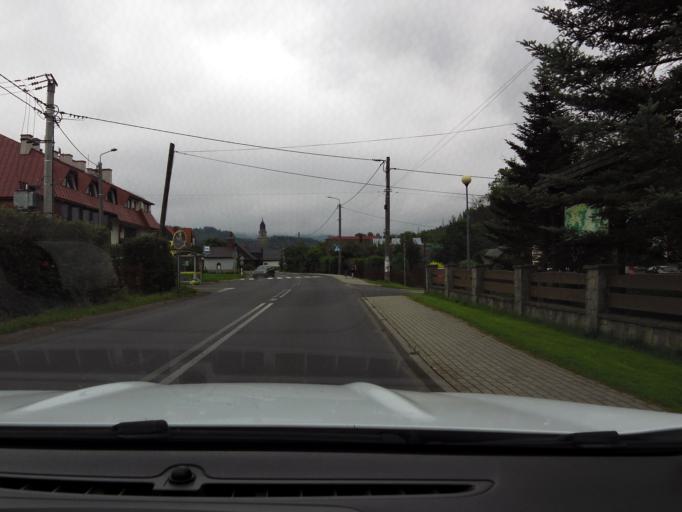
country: PL
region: Silesian Voivodeship
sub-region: Powiat zywiecki
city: Ujsoly
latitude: 49.4824
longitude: 19.1386
